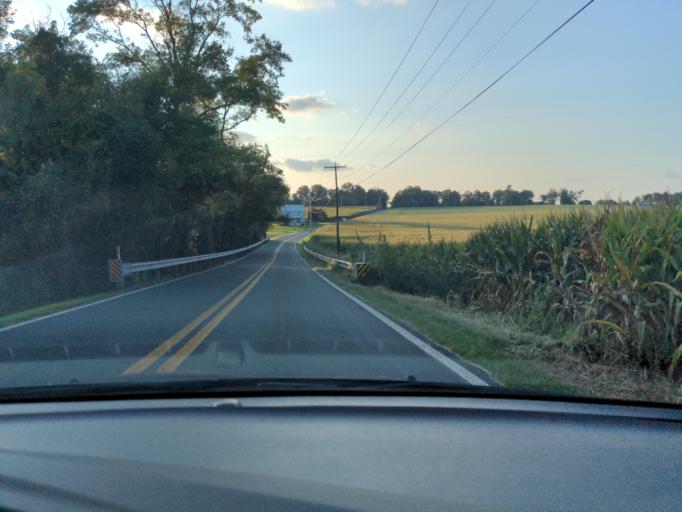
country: US
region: Maryland
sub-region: Carroll County
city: Hampstead
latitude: 39.5716
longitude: -76.8729
